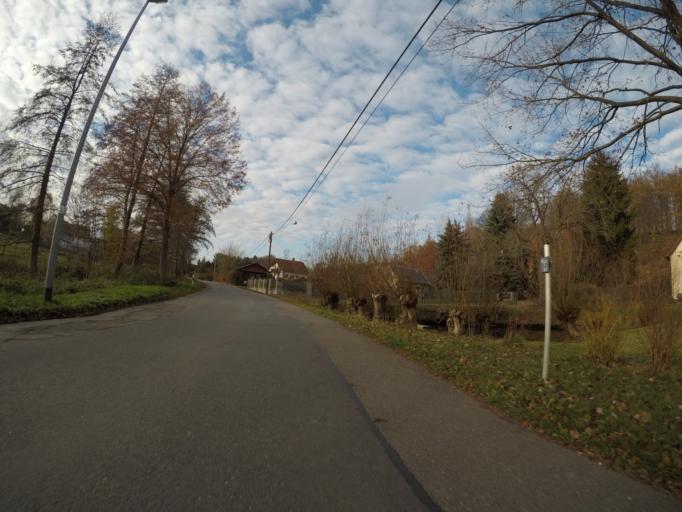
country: DE
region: Thuringia
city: Ponitz
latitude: 50.8584
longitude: 12.3915
